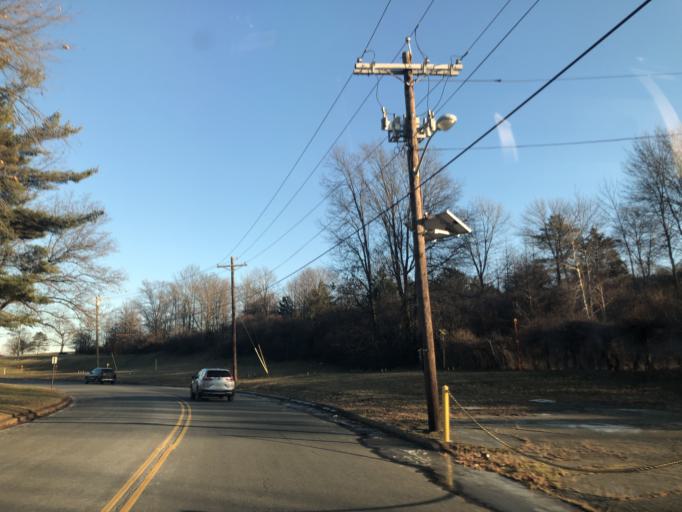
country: US
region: New Jersey
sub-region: Middlesex County
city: Woodbridge
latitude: 40.5447
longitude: -74.2940
